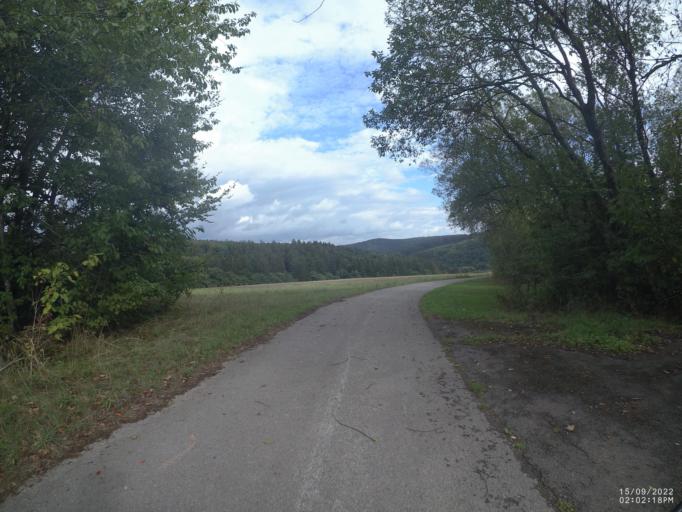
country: DE
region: Rheinland-Pfalz
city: Oberehe-Stroheich
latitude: 50.2847
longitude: 6.7645
